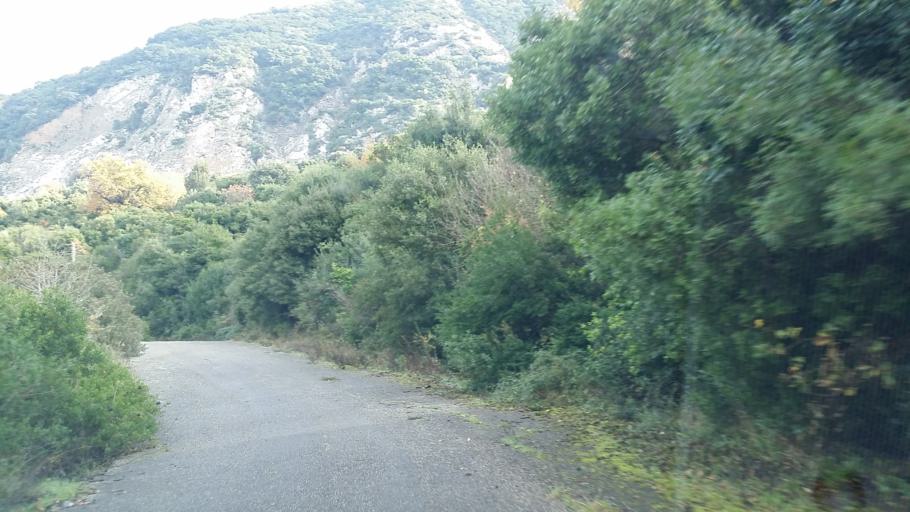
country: GR
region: West Greece
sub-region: Nomos Aitolias kai Akarnanias
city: Katouna
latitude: 38.8495
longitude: 21.0529
